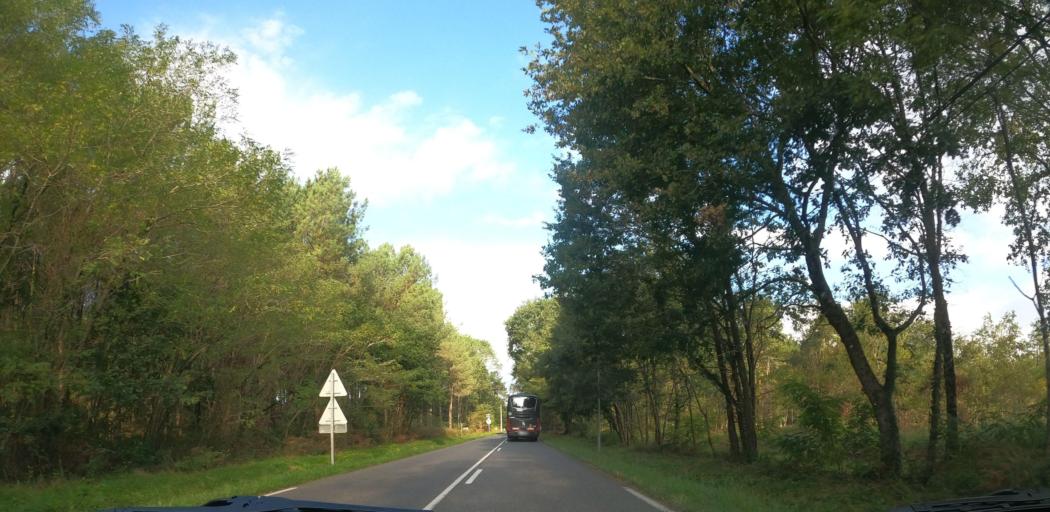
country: FR
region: Aquitaine
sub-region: Departement des Landes
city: Soustons
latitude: 43.7339
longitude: -1.2897
